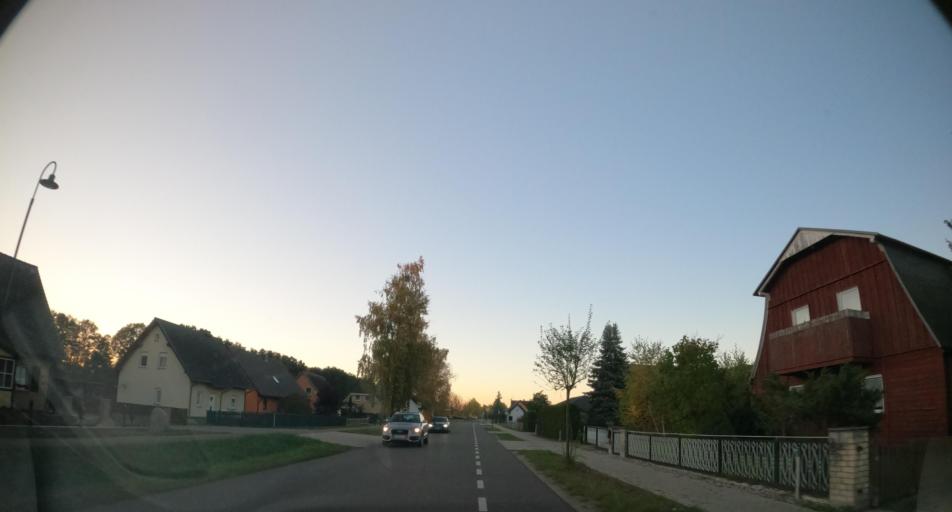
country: DE
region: Mecklenburg-Vorpommern
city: Ueckermunde
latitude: 53.7591
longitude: 14.0113
